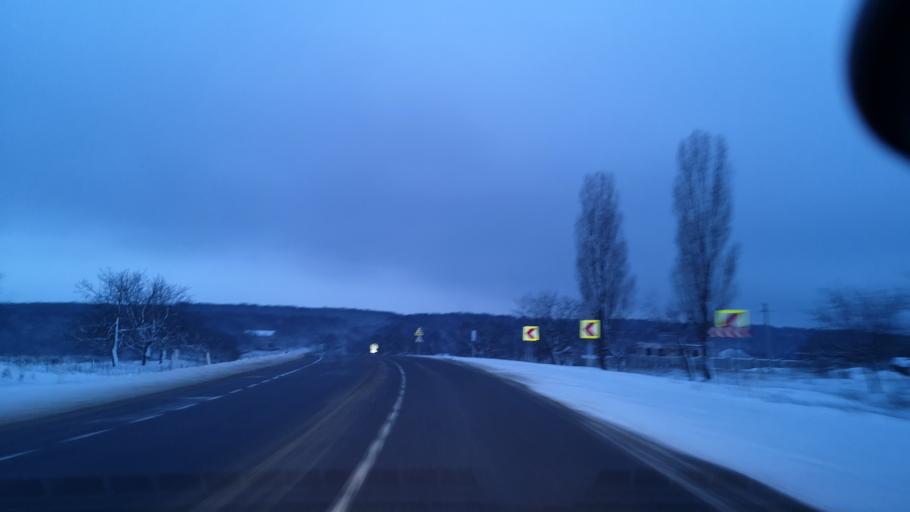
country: MD
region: Rezina
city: Rezina
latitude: 47.7354
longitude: 28.8786
